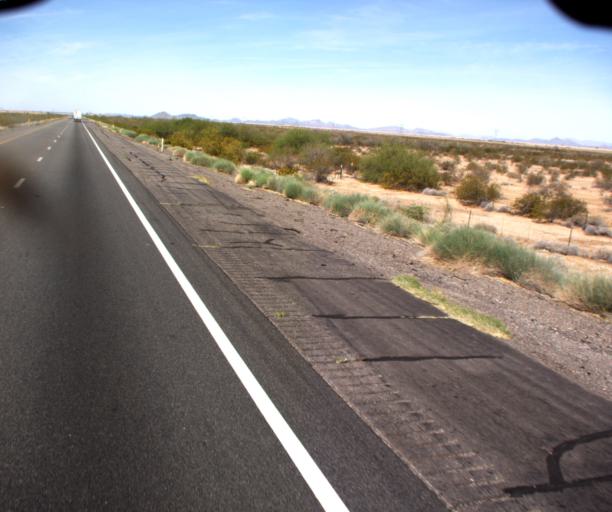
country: US
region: Arizona
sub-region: La Paz County
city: Salome
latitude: 33.5664
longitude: -113.3341
